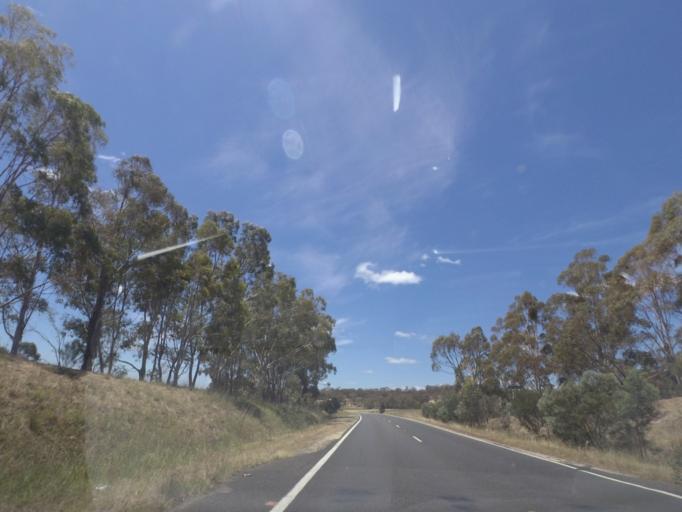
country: AU
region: Victoria
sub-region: Mount Alexander
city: Castlemaine
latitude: -37.1626
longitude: 144.1555
